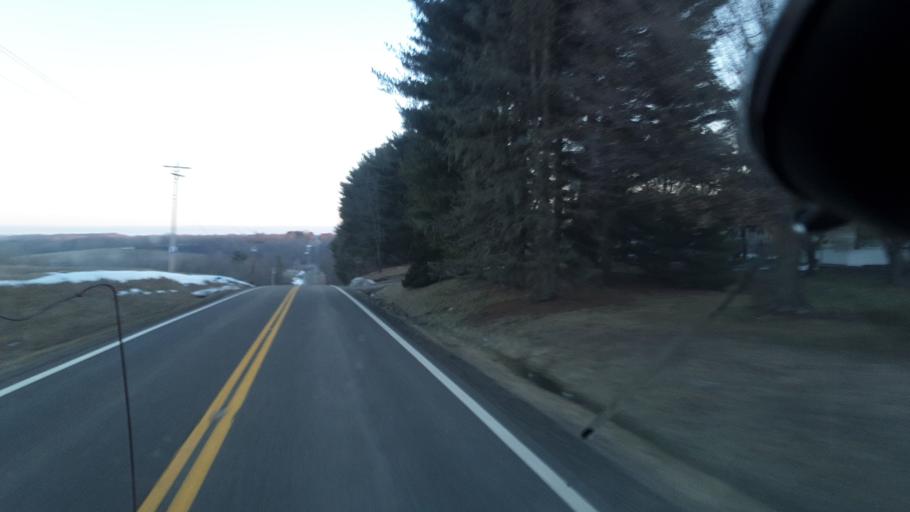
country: US
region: Ohio
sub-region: Perry County
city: Somerset
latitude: 39.7569
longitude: -82.3044
